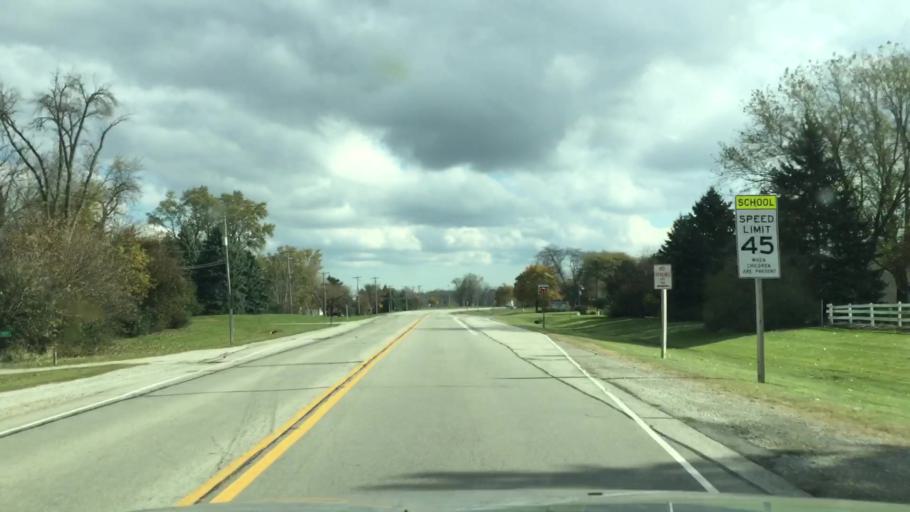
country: US
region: Wisconsin
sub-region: Racine County
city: Union Grove
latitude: 42.7423
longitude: -88.0452
